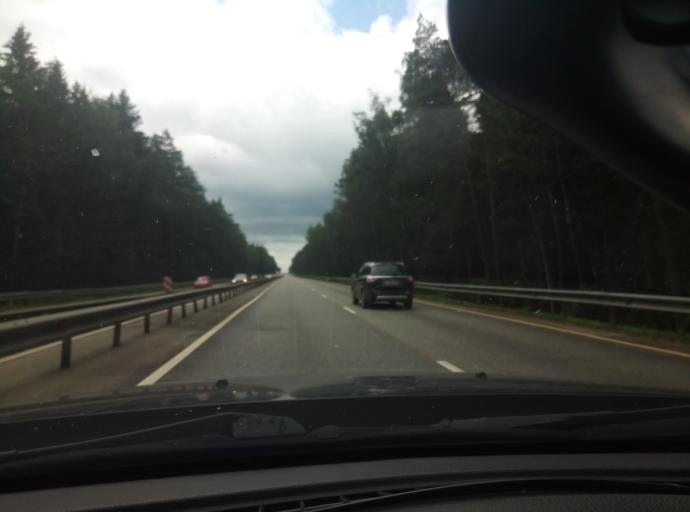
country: RU
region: Kaluga
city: Obninsk
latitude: 55.0259
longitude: 36.5699
